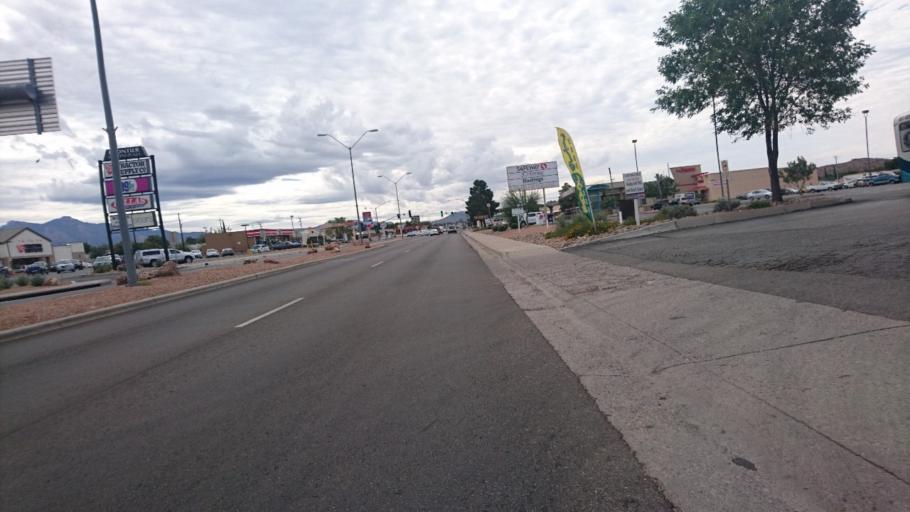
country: US
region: Arizona
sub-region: Mohave County
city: Kingman
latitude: 35.2156
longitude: -114.0354
